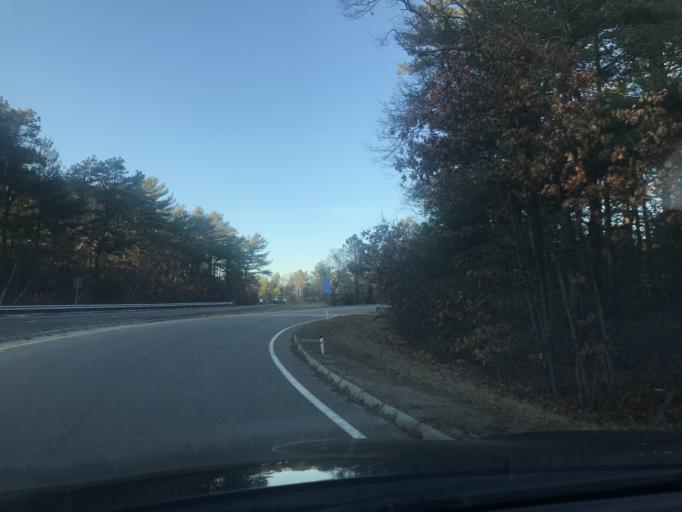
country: US
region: Massachusetts
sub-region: Plymouth County
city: Middleborough Center
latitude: 41.8821
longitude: -70.9238
